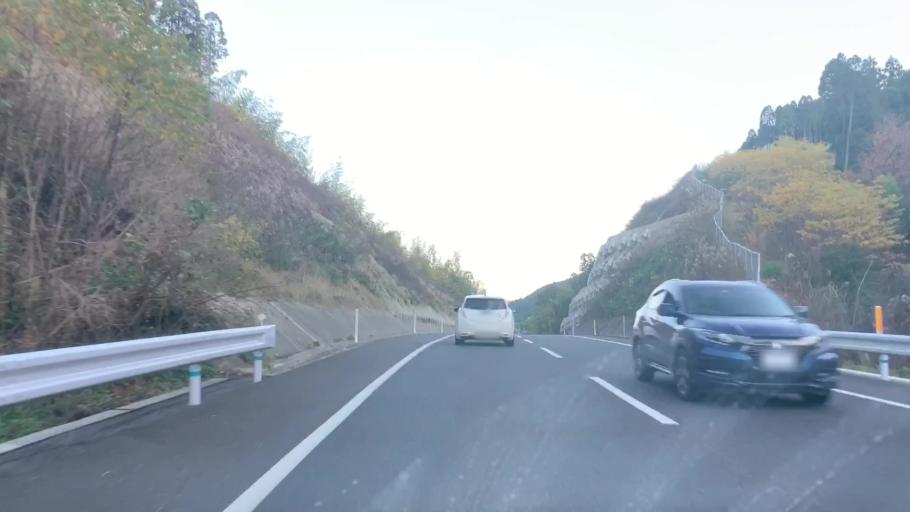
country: JP
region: Saga Prefecture
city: Takeocho-takeo
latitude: 33.2562
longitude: 129.9811
